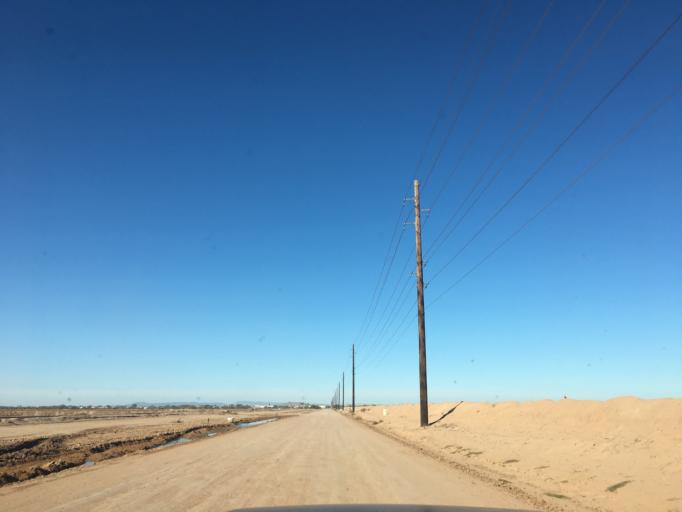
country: US
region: Arizona
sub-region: Pinal County
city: Maricopa
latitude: 33.0188
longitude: -112.0138
